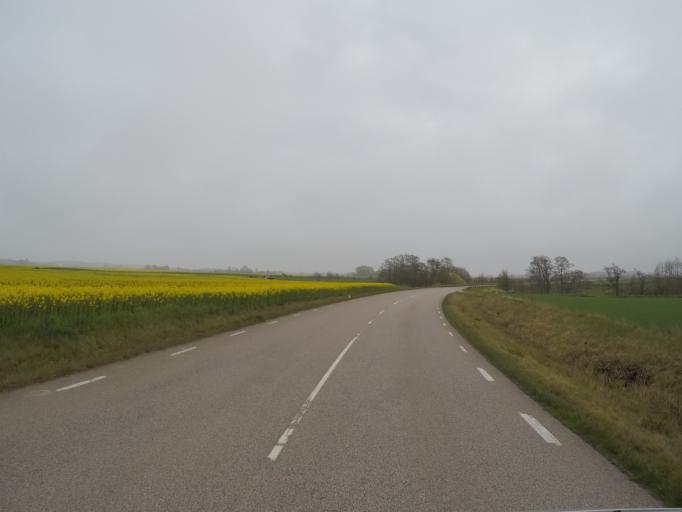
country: SE
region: Halland
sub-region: Laholms Kommun
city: Mellbystrand
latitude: 56.5415
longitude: 12.9757
